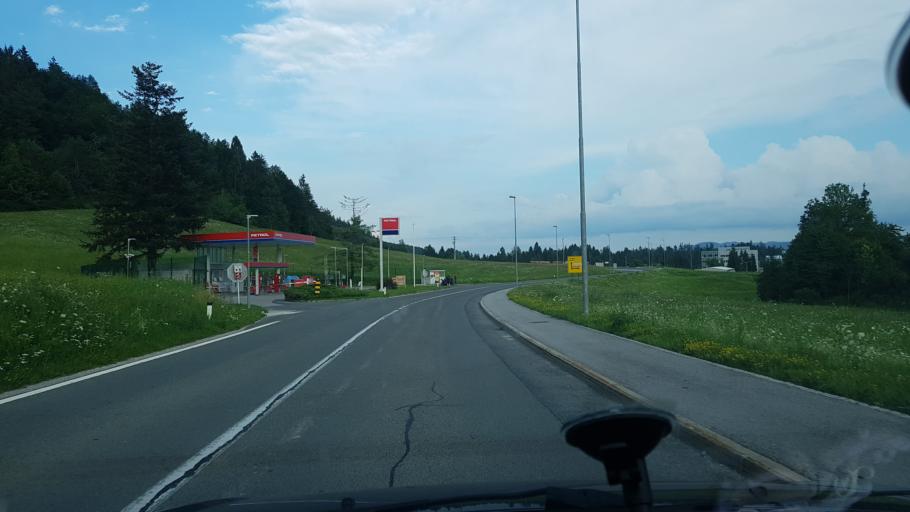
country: SI
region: Idrija
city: Idrija
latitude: 45.9569
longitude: 14.0934
